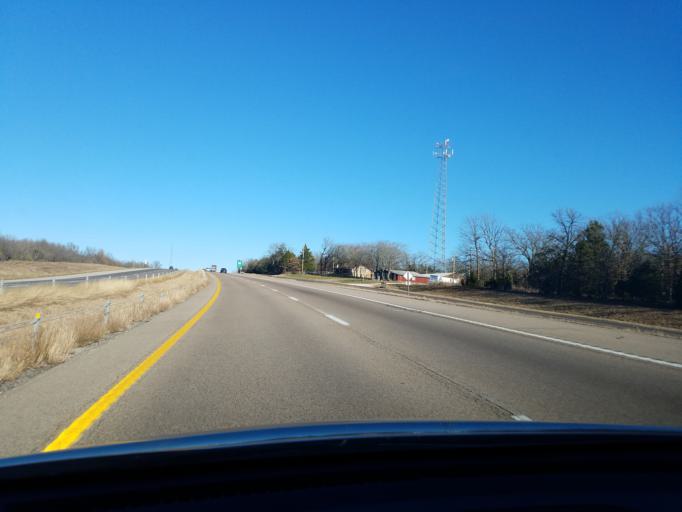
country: US
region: Missouri
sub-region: Pulaski County
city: Dixon
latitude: 37.8644
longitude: -92.0278
